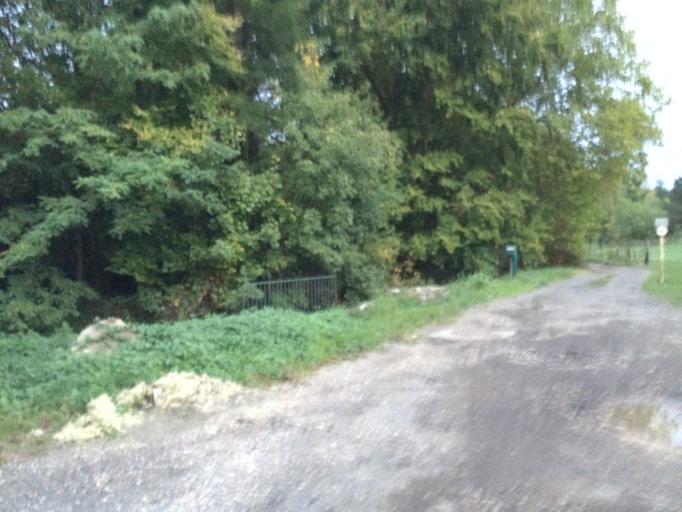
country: FR
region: Ile-de-France
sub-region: Departement des Yvelines
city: Velizy-Villacoublay
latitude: 48.7603
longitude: 2.1931
